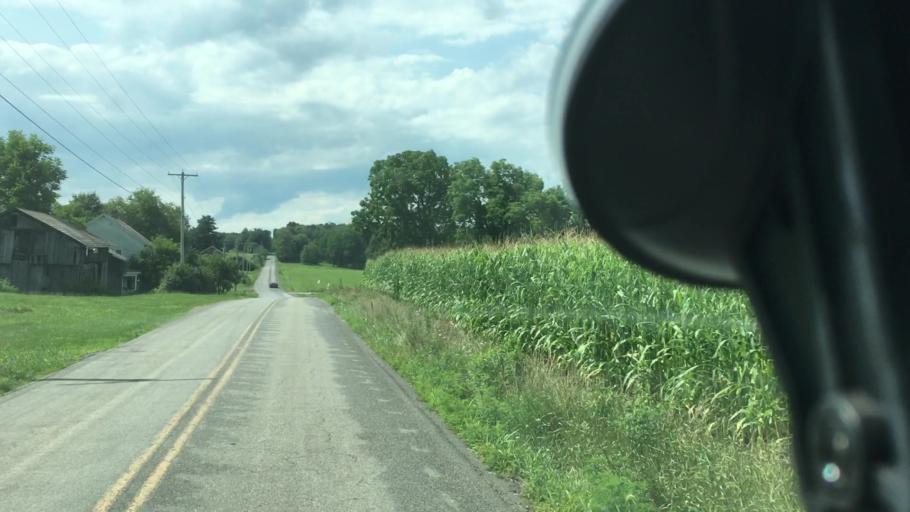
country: US
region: Pennsylvania
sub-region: Mercer County
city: Reynolds Heights
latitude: 41.3116
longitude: -80.3912
